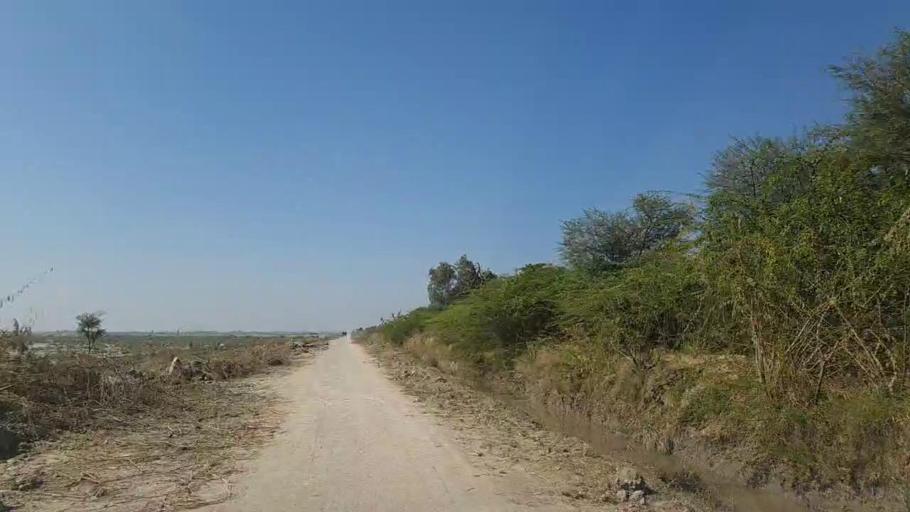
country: PK
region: Sindh
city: Pithoro
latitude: 25.4346
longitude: 69.3706
